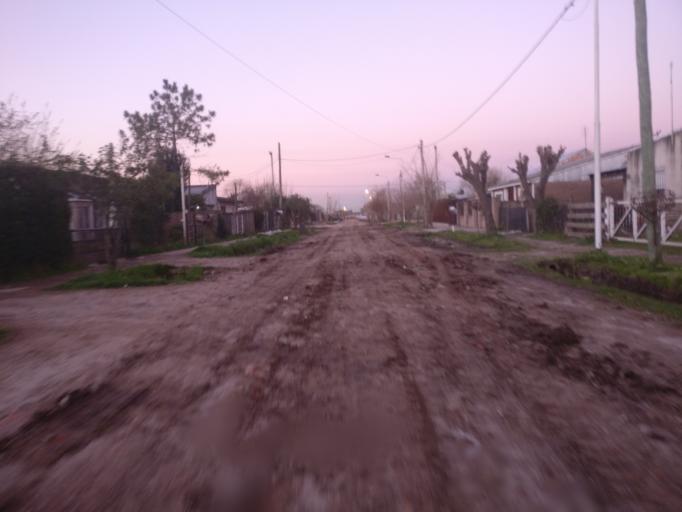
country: AR
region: Buenos Aires
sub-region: Partido de Ezeiza
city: Ezeiza
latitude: -34.9390
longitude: -58.6074
